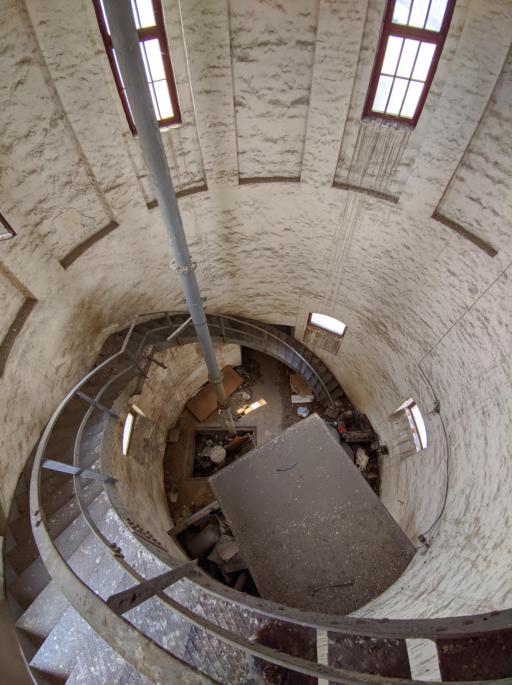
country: PL
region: Lower Silesian Voivodeship
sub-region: Powiat zabkowicki
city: Kamieniec Zabkowicki
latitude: 50.5367
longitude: 16.9019
